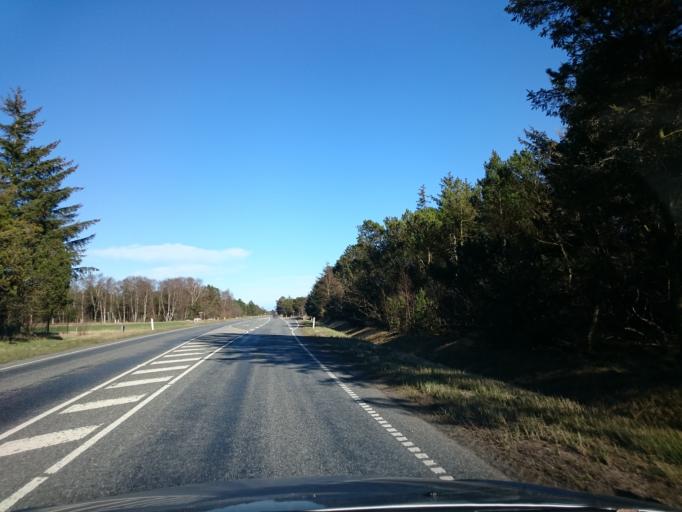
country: DK
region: North Denmark
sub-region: Frederikshavn Kommune
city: Strandby
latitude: 57.6067
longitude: 10.3935
